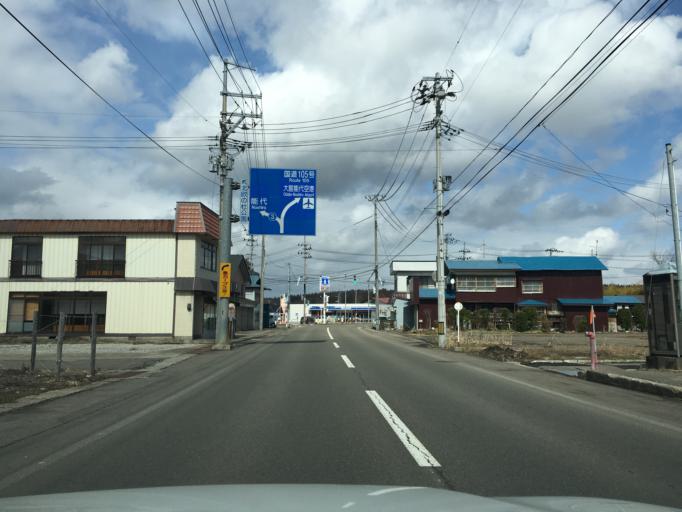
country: JP
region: Akita
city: Takanosu
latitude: 40.1227
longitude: 140.3672
